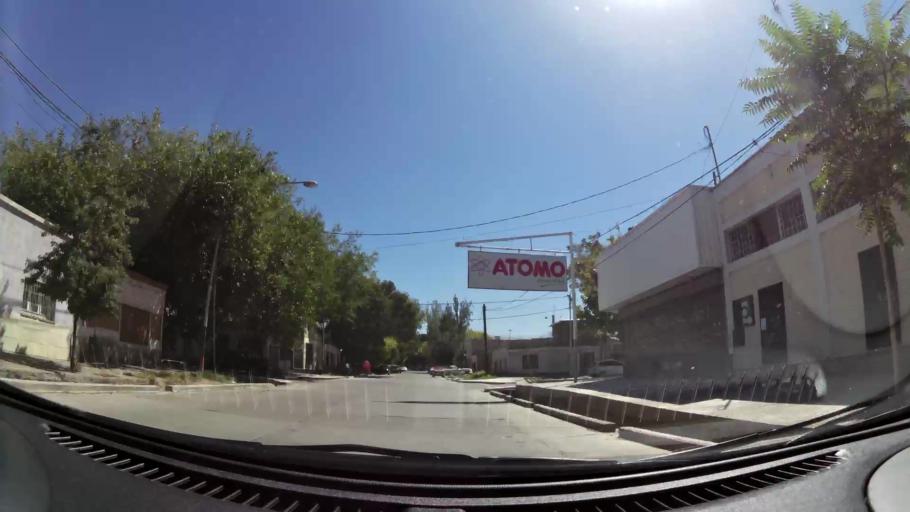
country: AR
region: Mendoza
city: Mendoza
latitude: -32.8762
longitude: -68.8191
